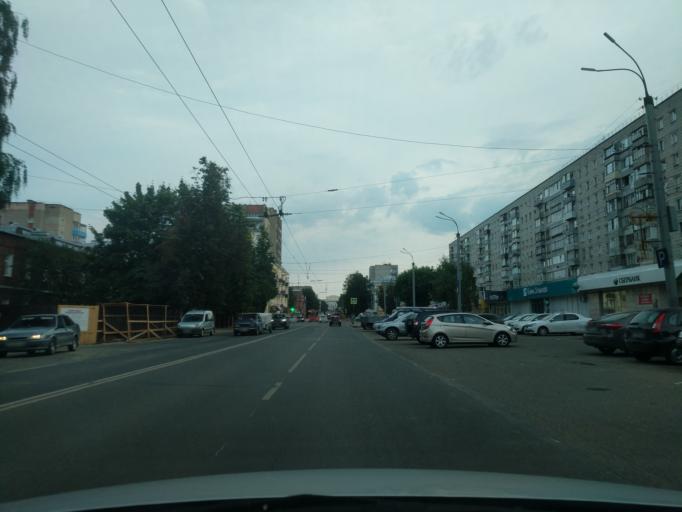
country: RU
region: Kirov
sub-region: Kirovo-Chepetskiy Rayon
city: Kirov
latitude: 58.6140
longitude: 49.6670
